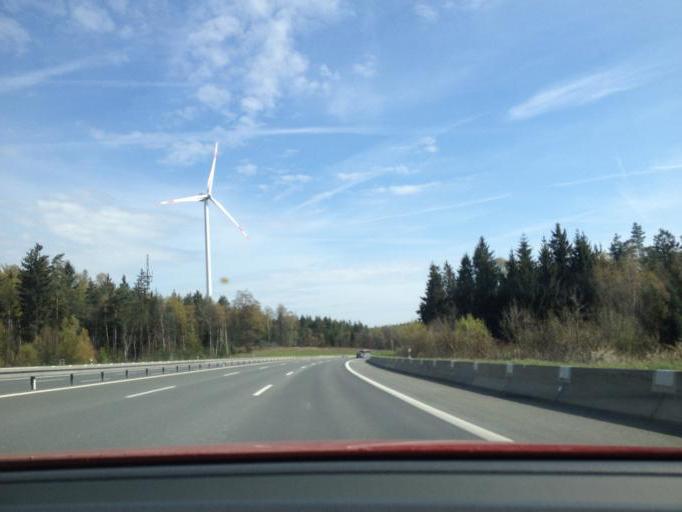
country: DE
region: Bavaria
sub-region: Upper Franconia
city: Gesees
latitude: 49.8663
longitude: 11.5188
